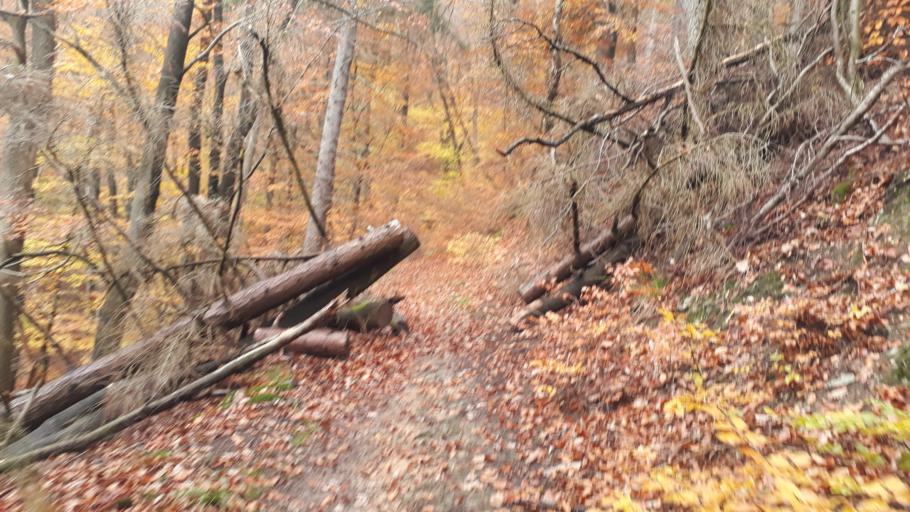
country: DE
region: Hesse
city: Willingen
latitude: 51.3696
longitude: 8.7323
